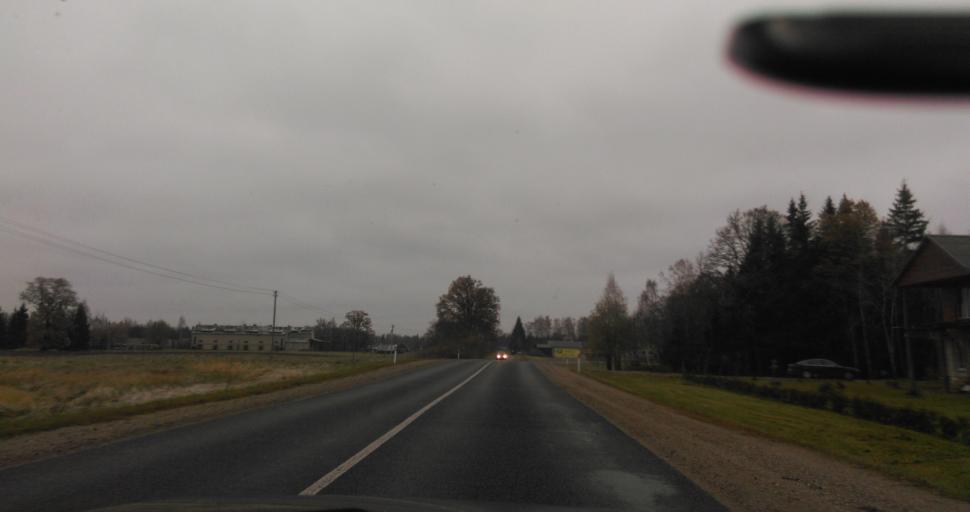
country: LT
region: Panevezys
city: Rokiskis
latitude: 55.9024
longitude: 25.5585
